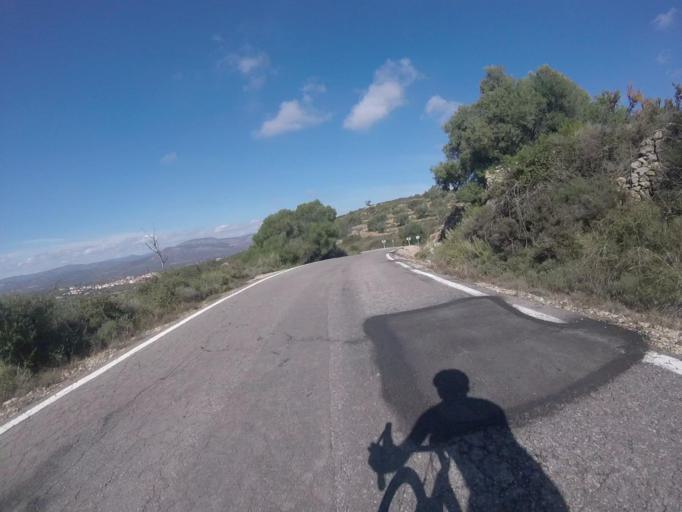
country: ES
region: Valencia
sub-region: Provincia de Castello
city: Albocasser
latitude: 40.3529
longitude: 0.0460
